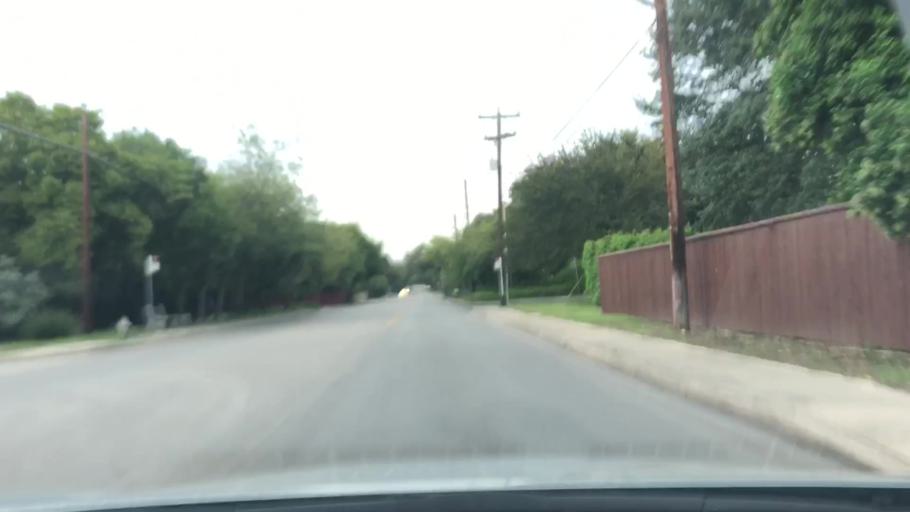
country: US
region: Texas
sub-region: Bexar County
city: Alamo Heights
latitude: 29.5082
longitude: -98.4570
